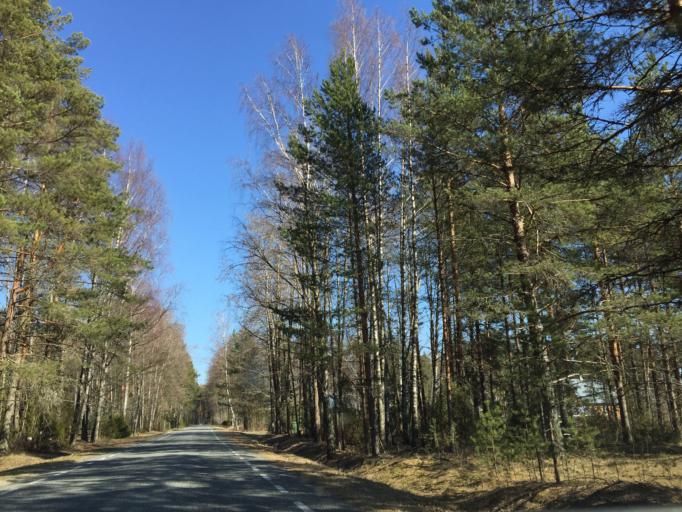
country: EE
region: Ida-Virumaa
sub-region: Johvi vald
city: Johvi
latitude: 59.0029
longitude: 27.3401
